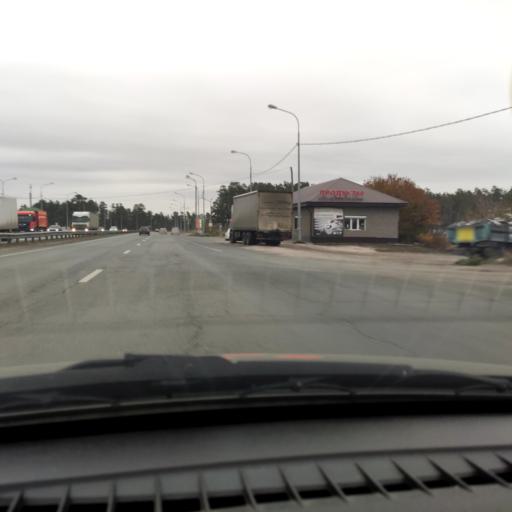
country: RU
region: Samara
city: Zhigulevsk
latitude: 53.5421
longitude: 49.5133
